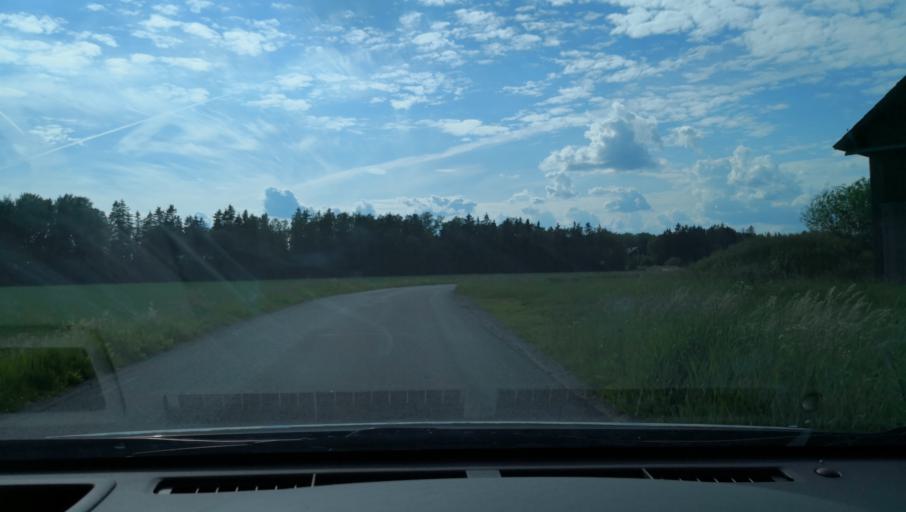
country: SE
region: Uppsala
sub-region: Enkopings Kommun
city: Irsta
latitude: 59.7525
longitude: 16.9578
